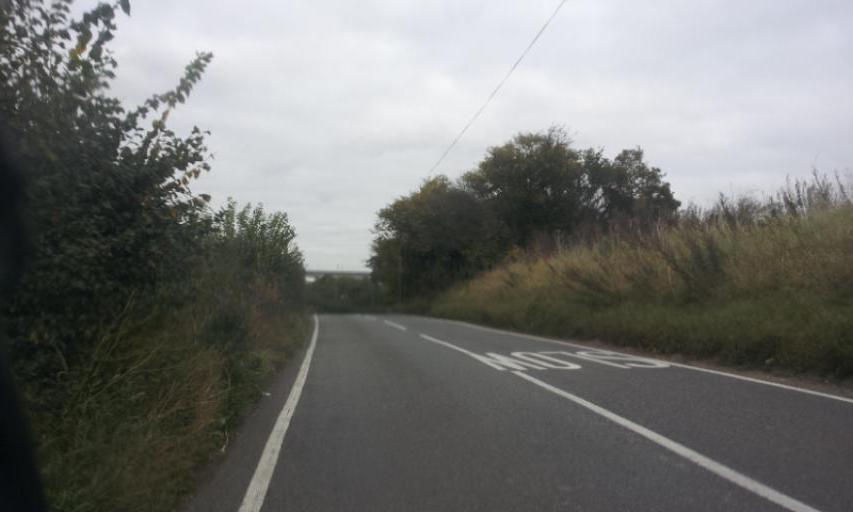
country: GB
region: England
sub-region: Medway
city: Cuxton
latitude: 51.3692
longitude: 0.4694
